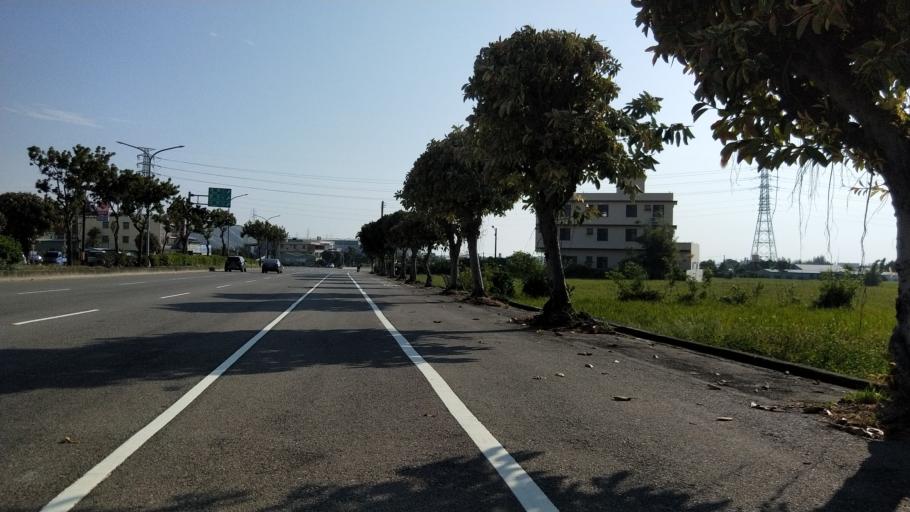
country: TW
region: Taiwan
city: Fengyuan
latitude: 24.3021
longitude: 120.5957
